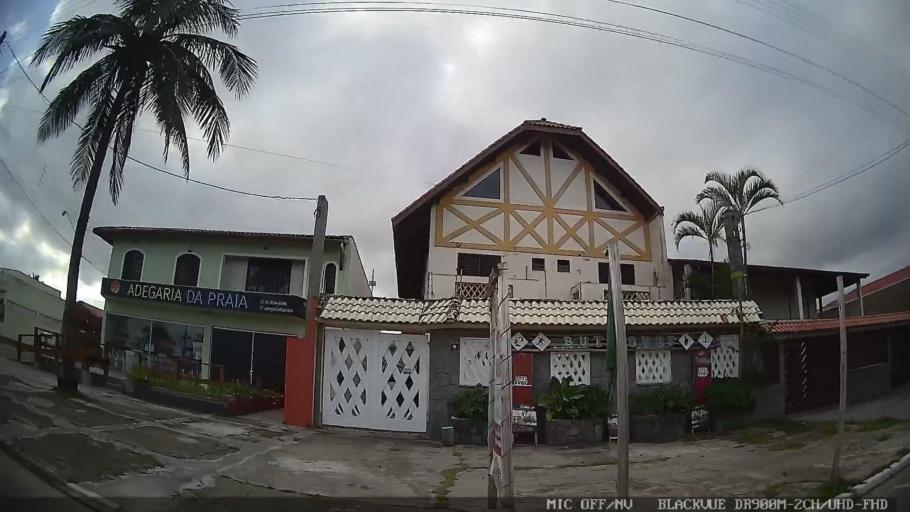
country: BR
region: Sao Paulo
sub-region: Peruibe
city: Peruibe
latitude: -24.3156
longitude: -46.9862
